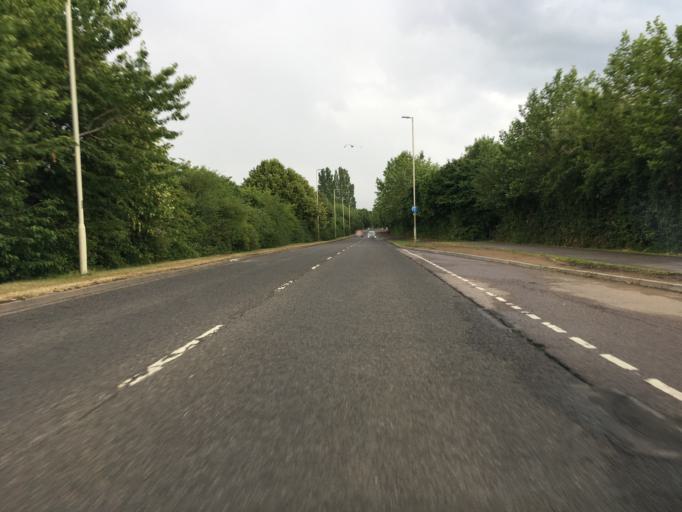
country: GB
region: England
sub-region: Gloucestershire
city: Barnwood
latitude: 51.8563
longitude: -2.2160
